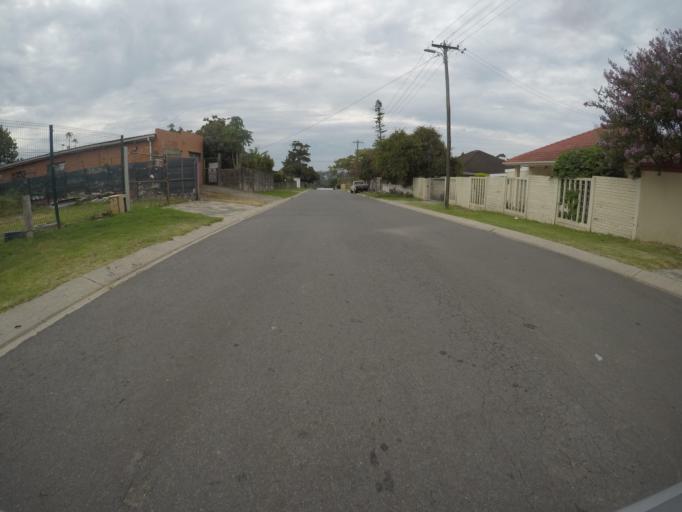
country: ZA
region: Eastern Cape
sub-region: Buffalo City Metropolitan Municipality
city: East London
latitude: -32.9966
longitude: 27.8750
